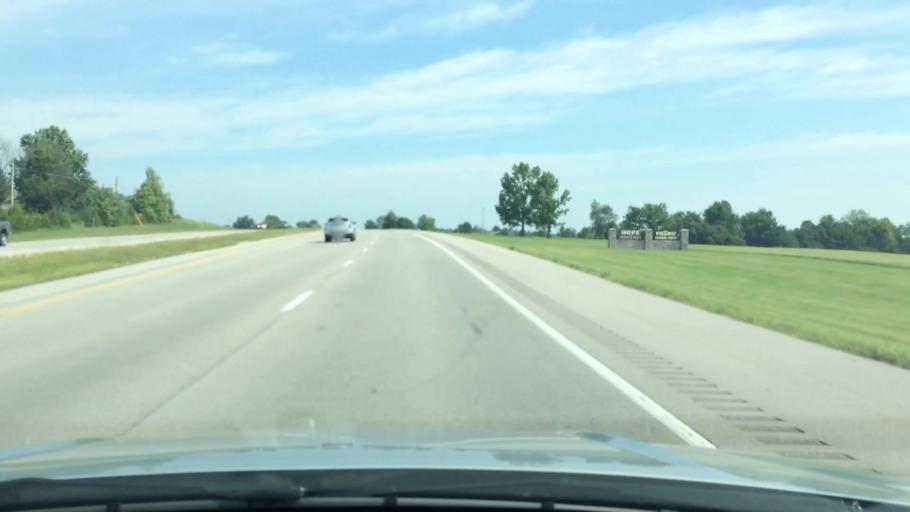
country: US
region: Kentucky
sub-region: Anderson County
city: Lawrenceburg
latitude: 38.1050
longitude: -84.9163
